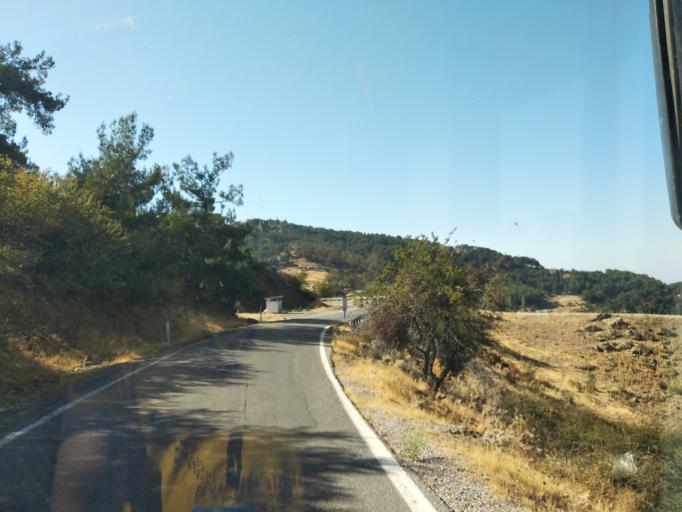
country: TR
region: Izmir
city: Gaziemir
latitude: 38.3249
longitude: 27.0060
